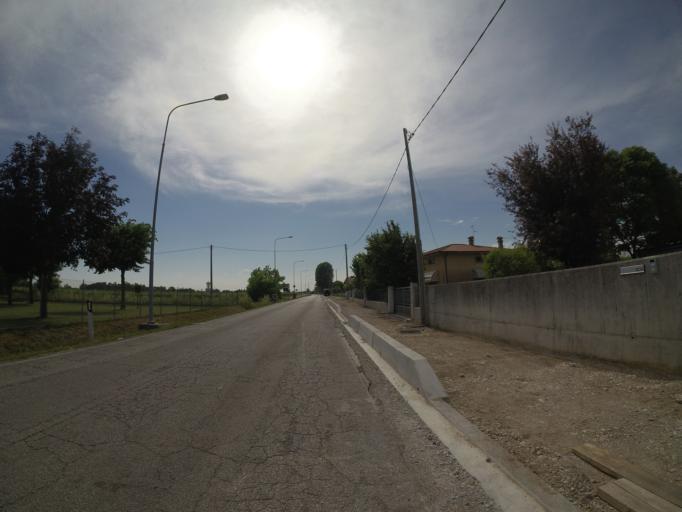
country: IT
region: Friuli Venezia Giulia
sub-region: Provincia di Udine
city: Codroipo
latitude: 45.9595
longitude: 12.9602
